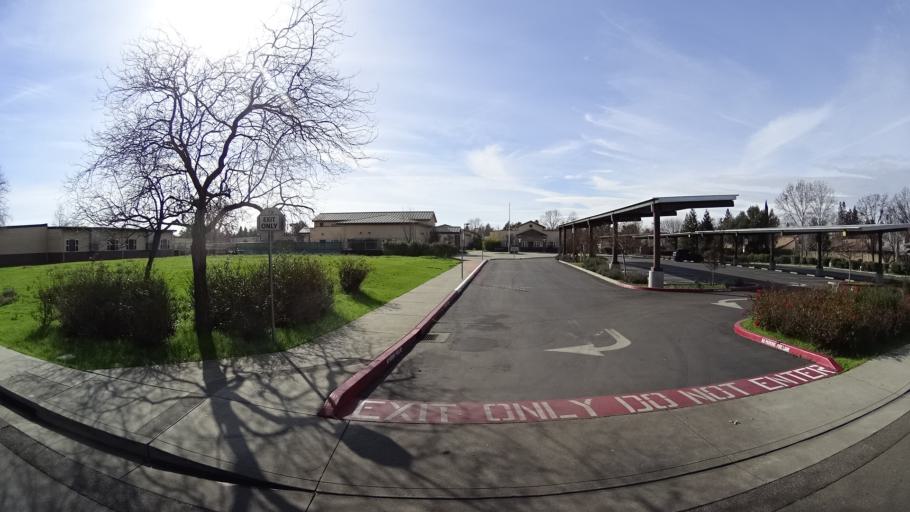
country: US
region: California
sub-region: Yolo County
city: Davis
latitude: 38.5594
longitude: -121.7084
